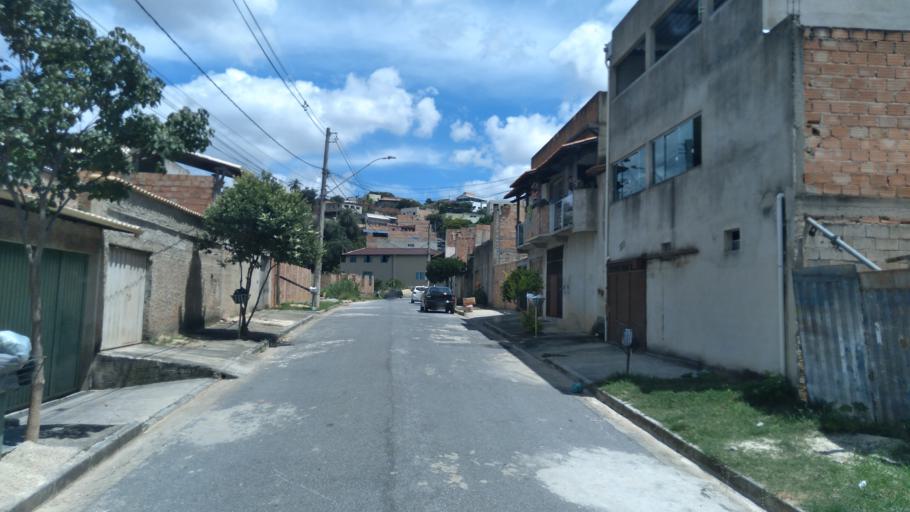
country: BR
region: Minas Gerais
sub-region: Santa Luzia
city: Santa Luzia
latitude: -19.8533
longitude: -43.8782
